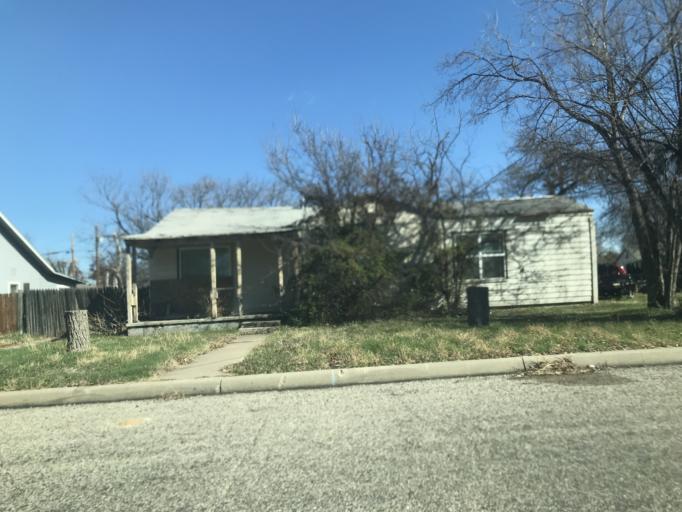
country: US
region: Texas
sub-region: Tom Green County
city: San Angelo
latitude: 31.4455
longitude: -100.4586
